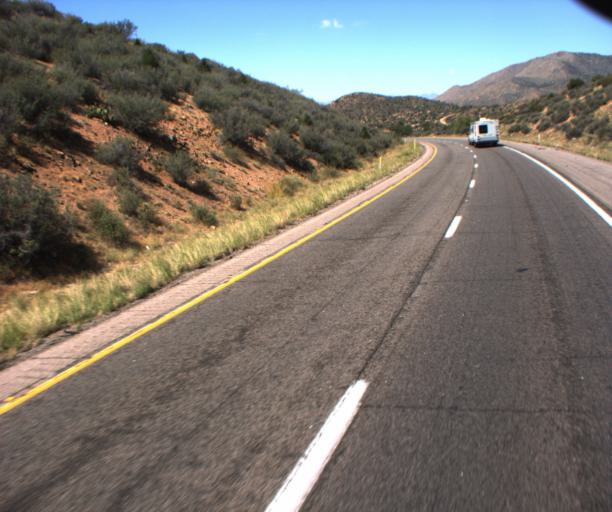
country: US
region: Arizona
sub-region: Mohave County
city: Peach Springs
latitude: 35.1791
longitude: -113.4929
